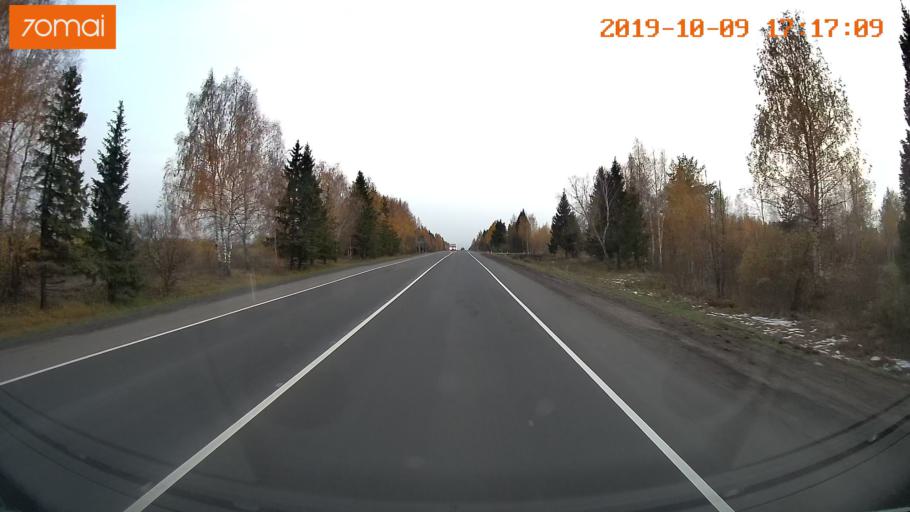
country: RU
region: Ivanovo
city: Furmanov
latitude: 57.2799
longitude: 41.1589
